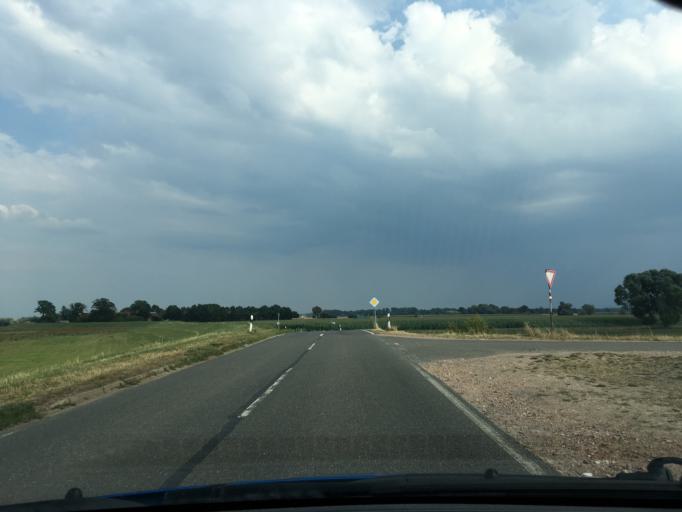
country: DE
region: Lower Saxony
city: Hitzacker
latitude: 53.1397
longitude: 11.0697
